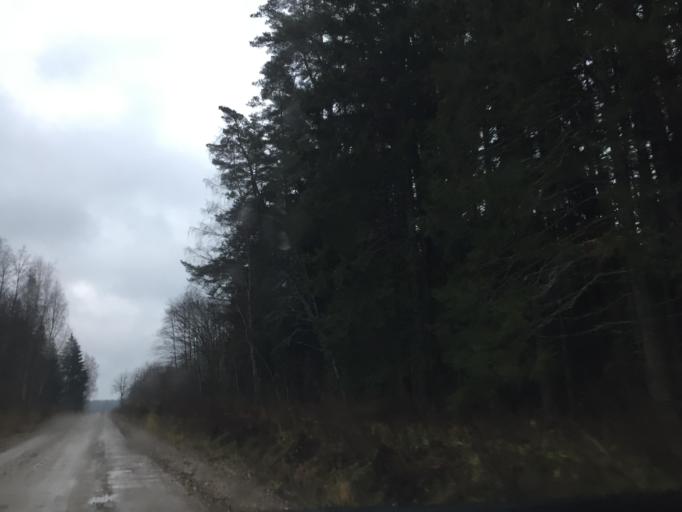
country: LV
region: Aloja
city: Staicele
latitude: 57.7566
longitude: 24.6143
